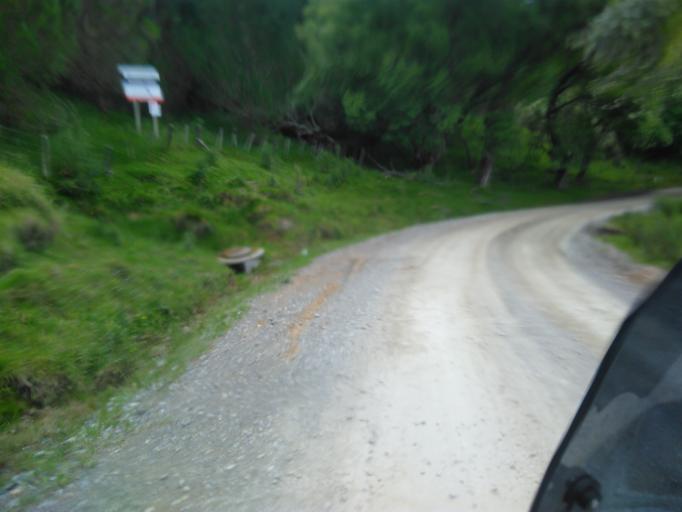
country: NZ
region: Gisborne
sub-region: Gisborne District
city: Gisborne
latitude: -38.0942
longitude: 178.0903
